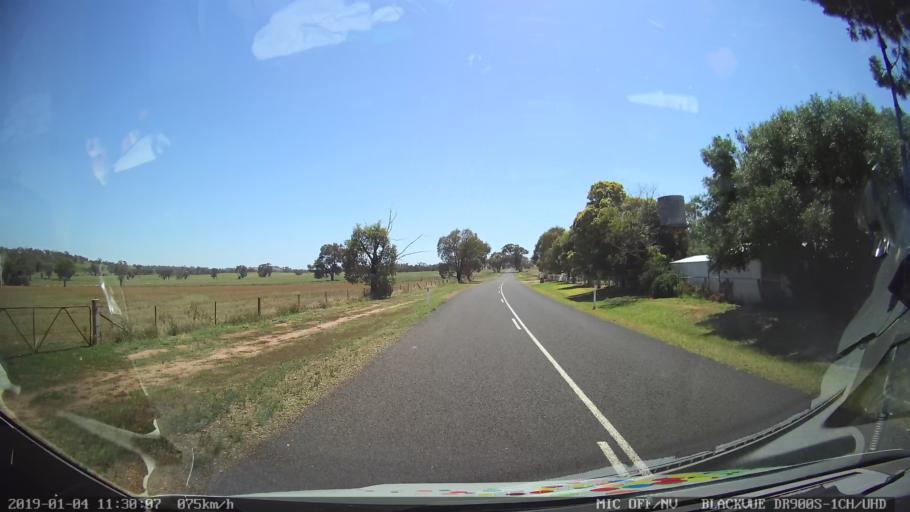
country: AU
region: New South Wales
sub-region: Cabonne
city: Molong
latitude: -33.0804
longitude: 148.7777
